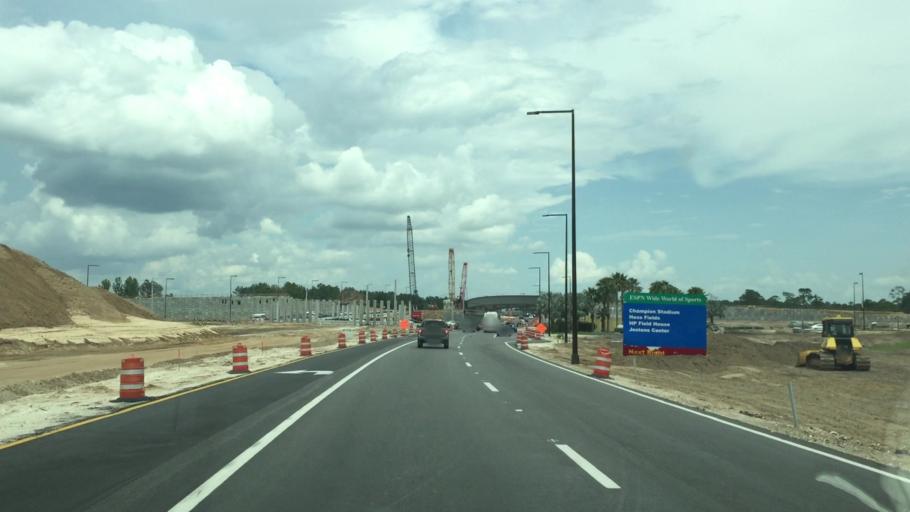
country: US
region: Florida
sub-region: Osceola County
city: Celebration
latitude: 28.3480
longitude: -81.5551
